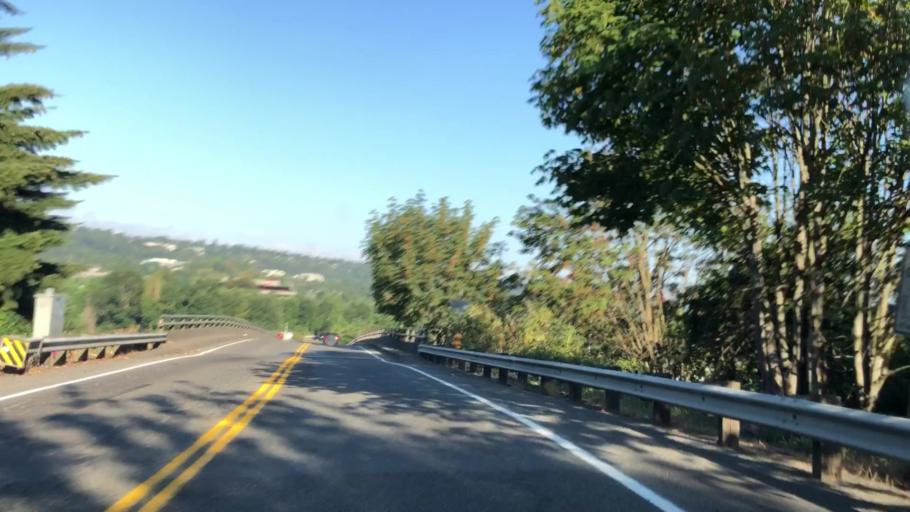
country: US
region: Washington
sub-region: King County
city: Tukwila
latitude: 47.4890
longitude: -122.2636
